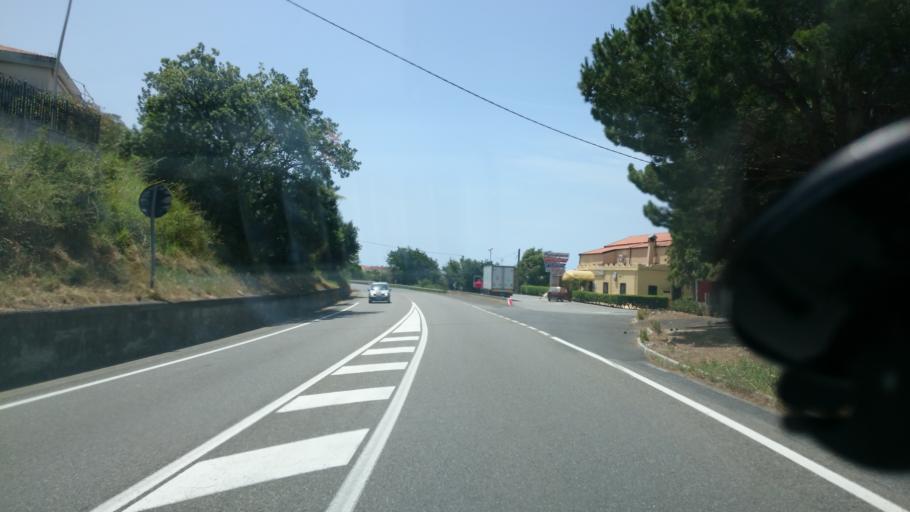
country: IT
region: Calabria
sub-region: Provincia di Cosenza
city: Cittadella del Capo
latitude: 39.5796
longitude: 15.8695
